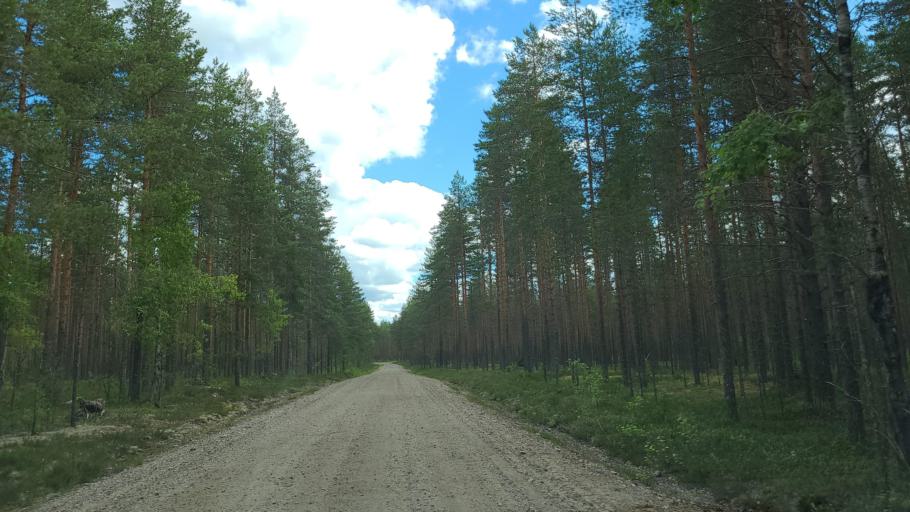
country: FI
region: Northern Savo
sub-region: Koillis-Savo
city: Kaavi
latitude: 63.0522
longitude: 28.8162
